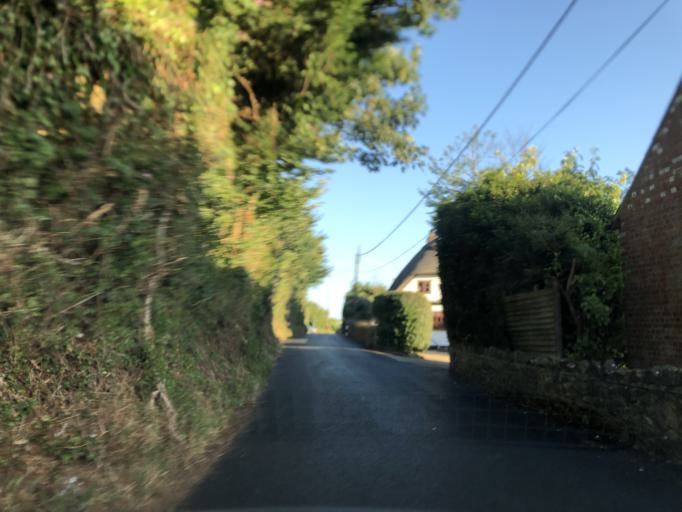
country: GB
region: England
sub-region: Isle of Wight
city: Shalfleet
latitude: 50.6479
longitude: -1.4007
